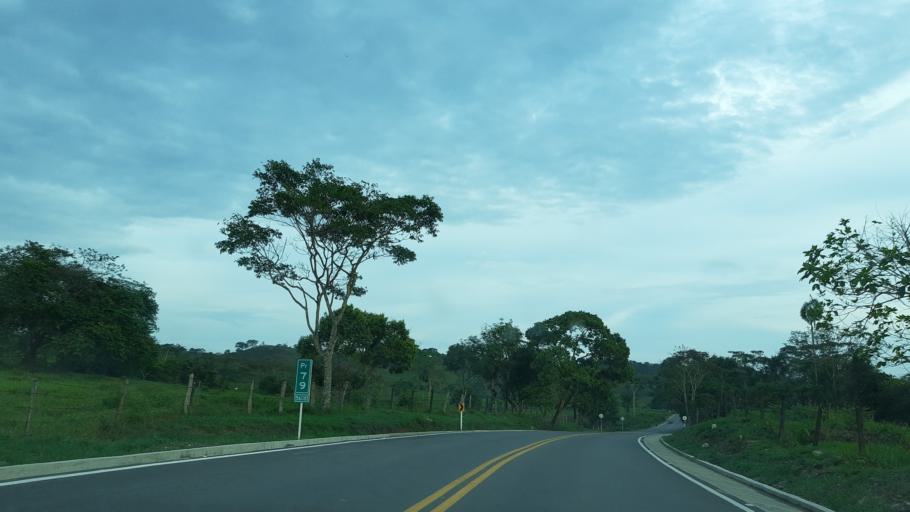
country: CO
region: Casanare
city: Sabanalarga
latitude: 4.8165
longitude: -73.0642
